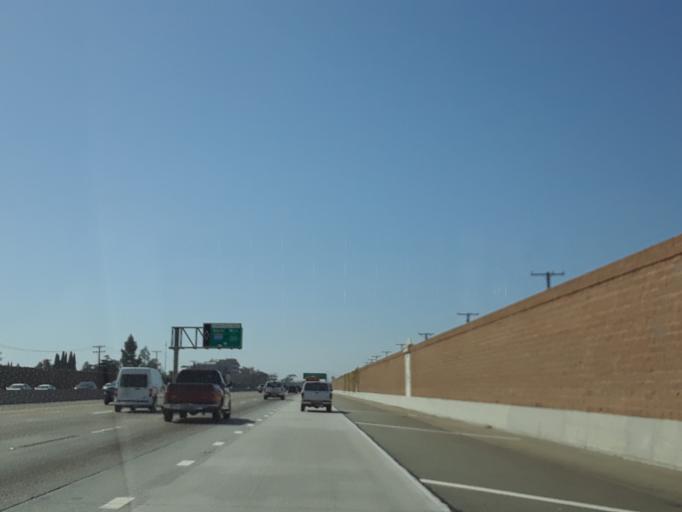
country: US
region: California
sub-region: Orange County
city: Westminster
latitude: 33.7745
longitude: -118.0264
